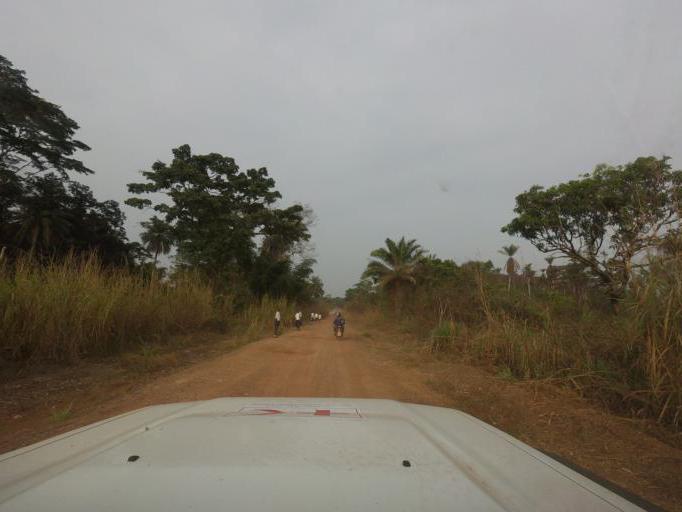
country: LR
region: Lofa
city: Voinjama
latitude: 8.3690
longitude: -9.9082
